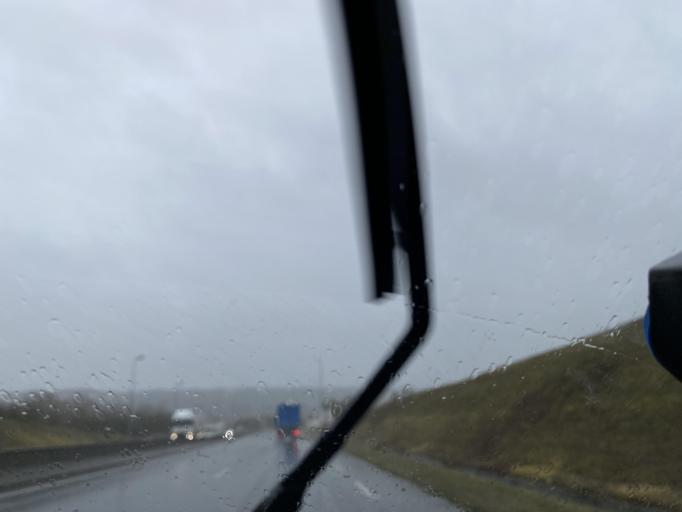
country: FR
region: Centre
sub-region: Departement d'Eure-et-Loir
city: Garnay
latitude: 48.7216
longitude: 1.3470
